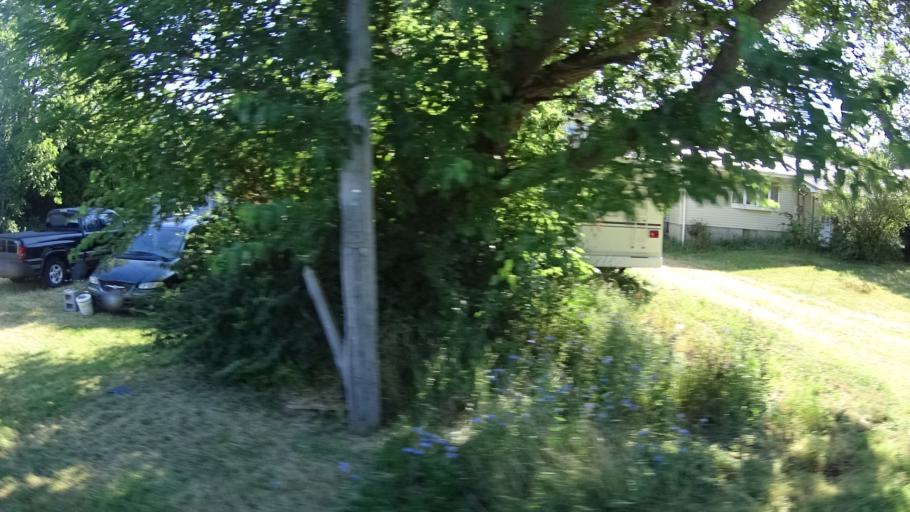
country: US
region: Ohio
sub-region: Erie County
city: Sandusky
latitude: 41.3631
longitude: -82.7602
